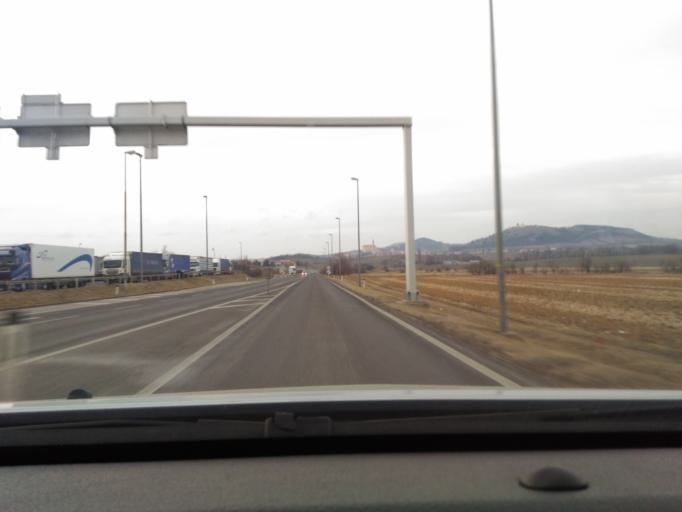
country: CZ
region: South Moravian
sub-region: Okres Breclav
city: Mikulov
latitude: 48.7813
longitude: 16.6398
